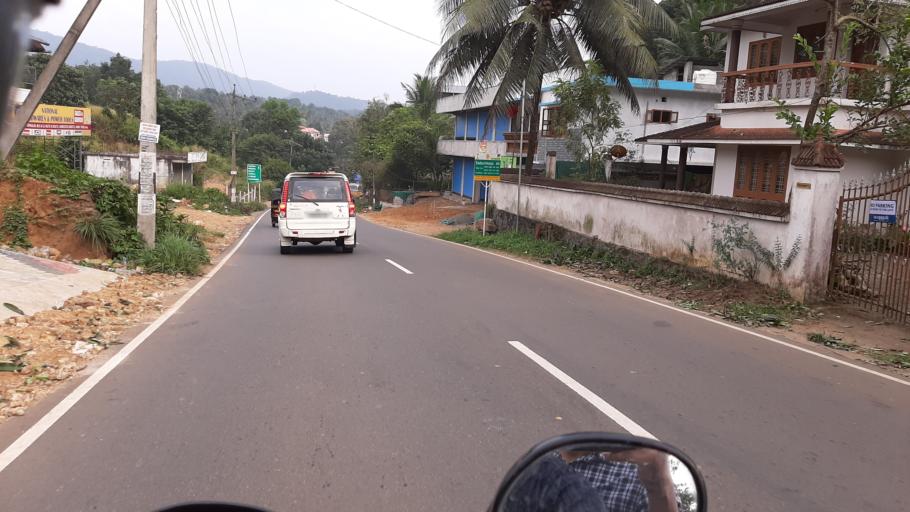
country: IN
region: Kerala
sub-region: Pattanamtitta
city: Pathanamthitta
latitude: 9.4474
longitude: 76.8745
